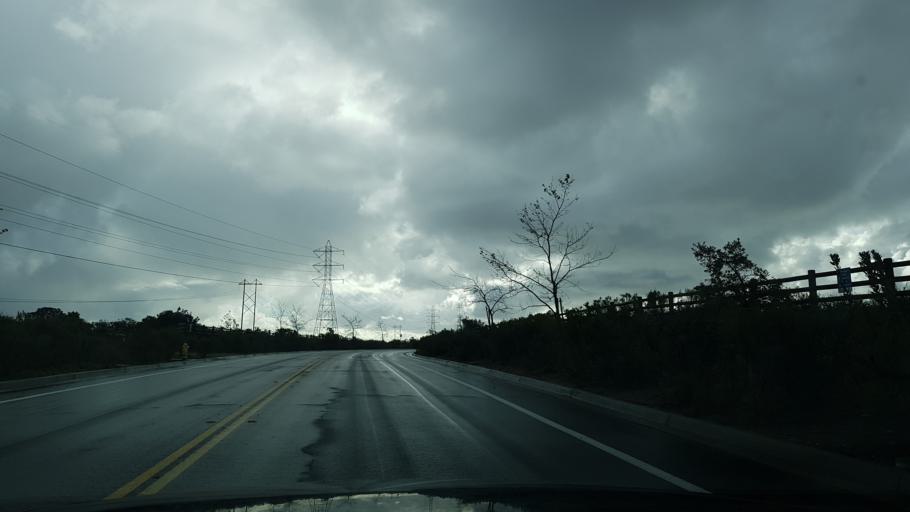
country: US
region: California
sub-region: San Diego County
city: Fairbanks Ranch
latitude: 32.9314
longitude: -117.1848
